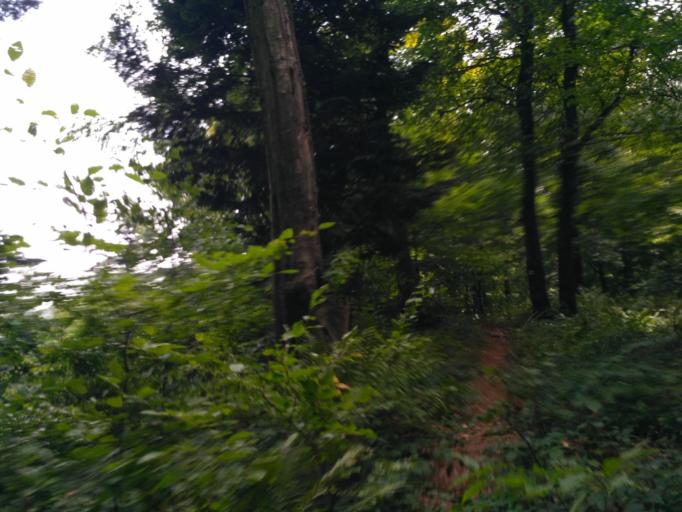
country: PL
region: Subcarpathian Voivodeship
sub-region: Powiat strzyzowski
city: Frysztak
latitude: 49.8860
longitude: 21.5445
